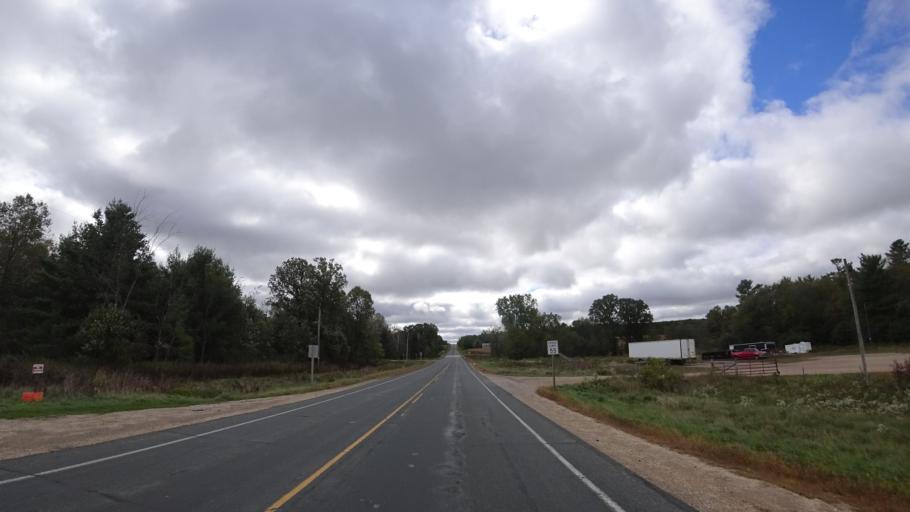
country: US
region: Wisconsin
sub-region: Saint Croix County
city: Woodville
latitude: 44.9323
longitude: -92.2783
